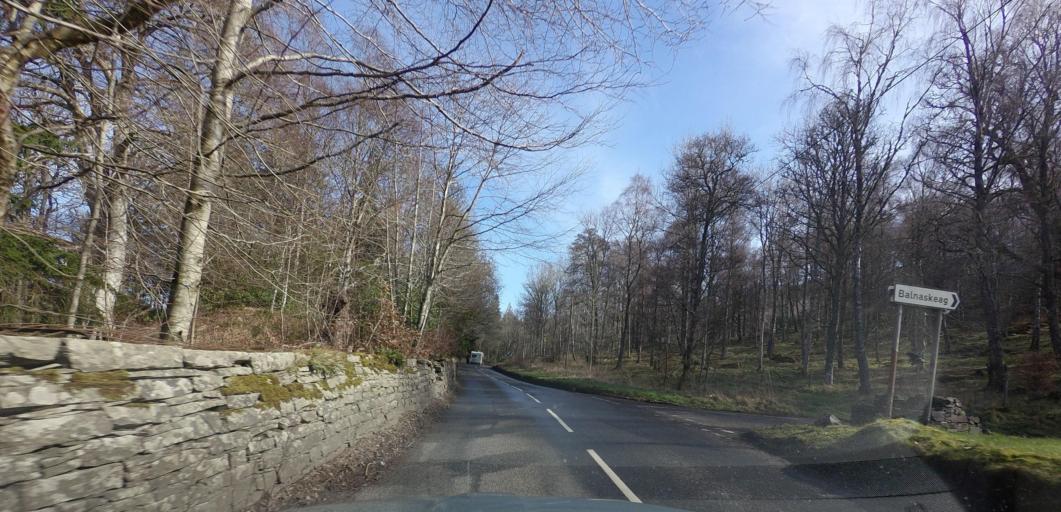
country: GB
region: Scotland
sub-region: Perth and Kinross
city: Aberfeldy
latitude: 56.5830
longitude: -3.9884
